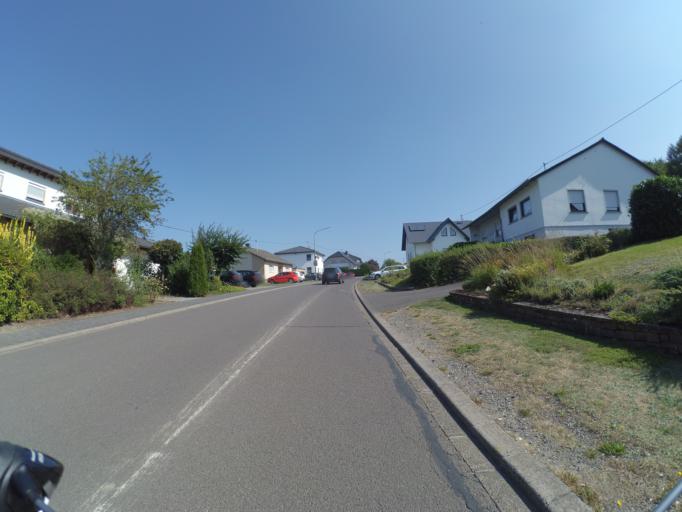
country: DE
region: Rheinland-Pfalz
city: Rorodt
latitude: 49.7709
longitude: 7.0903
